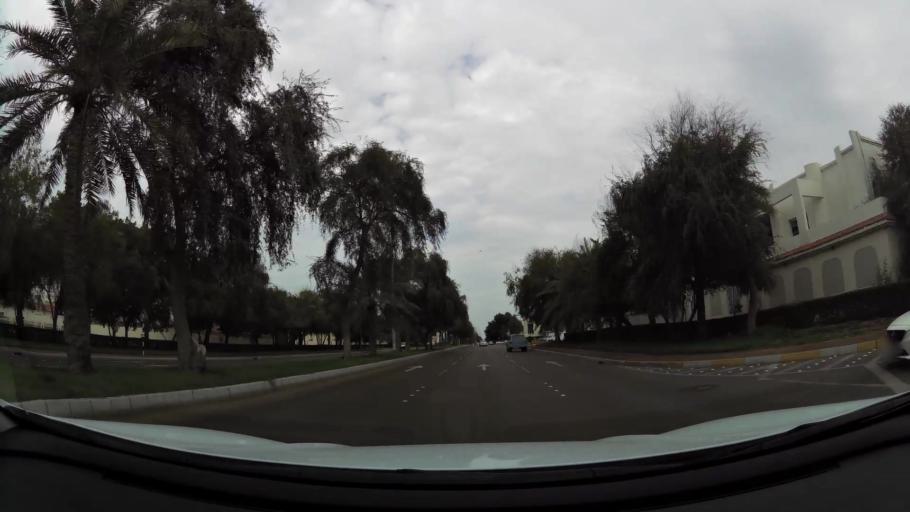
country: AE
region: Abu Dhabi
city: Abu Dhabi
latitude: 24.4286
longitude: 54.4010
